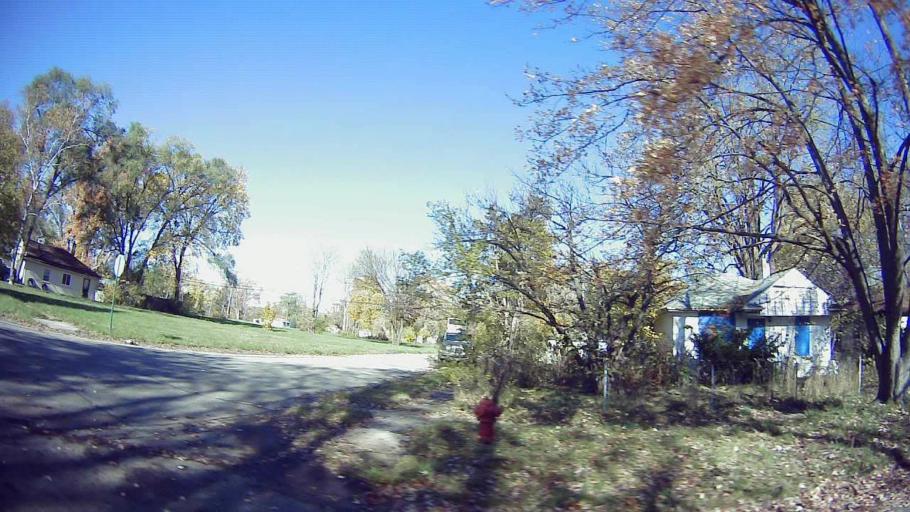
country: US
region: Michigan
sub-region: Wayne County
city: Redford
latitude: 42.3933
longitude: -83.2466
